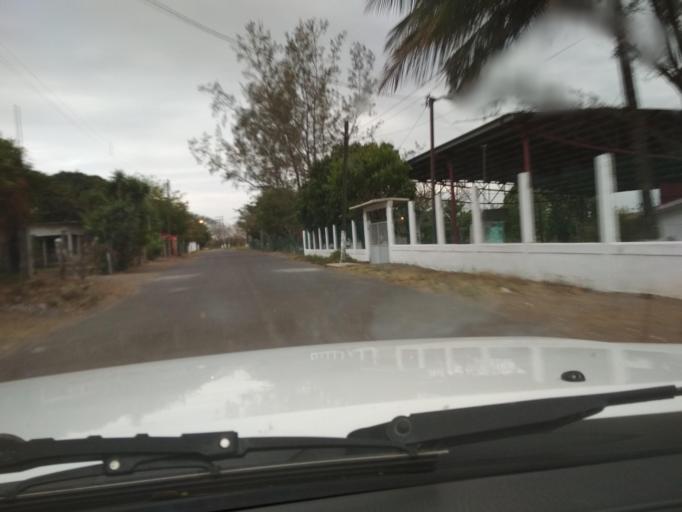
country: MX
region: Veracruz
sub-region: Veracruz
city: Delfino Victoria (Santa Fe)
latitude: 19.1628
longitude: -96.2608
